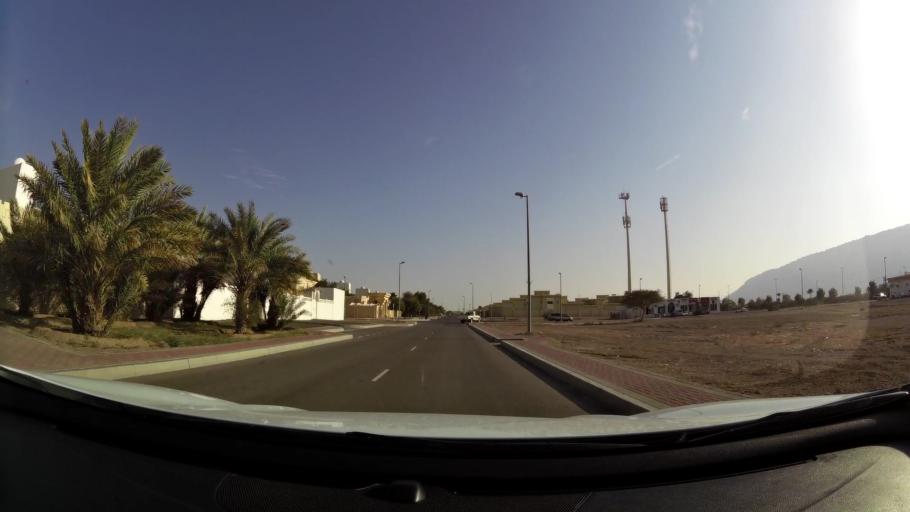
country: AE
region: Abu Dhabi
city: Al Ain
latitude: 24.0605
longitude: 55.8404
